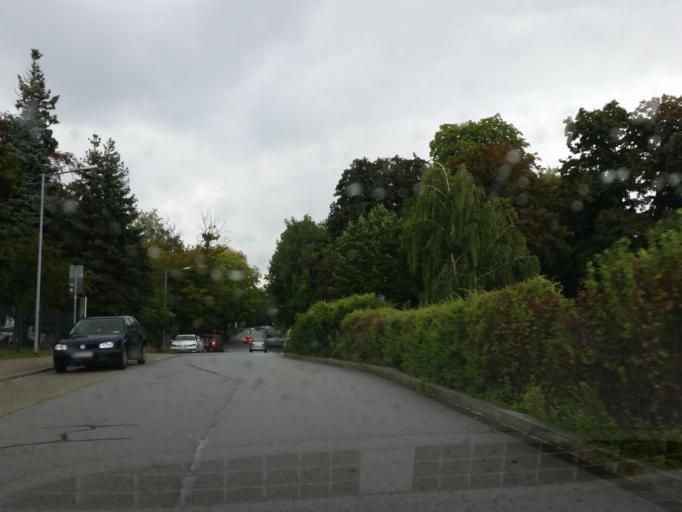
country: DE
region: Saxony
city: Bautzen
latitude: 51.1848
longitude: 14.4261
